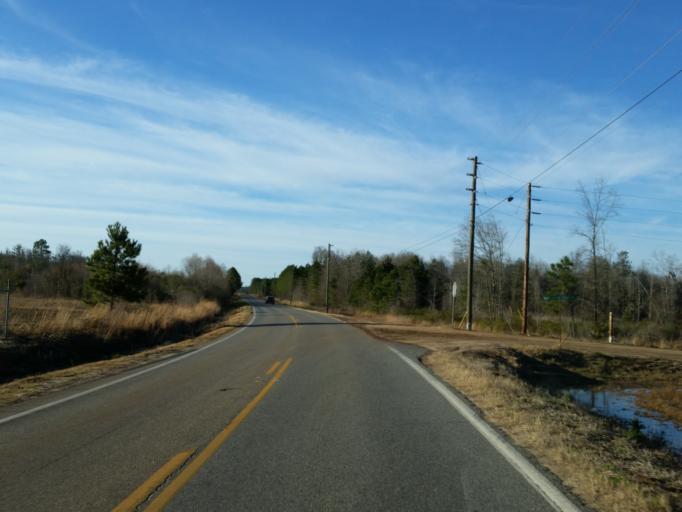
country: US
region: Georgia
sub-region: Cook County
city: Adel
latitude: 31.0753
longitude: -83.3986
